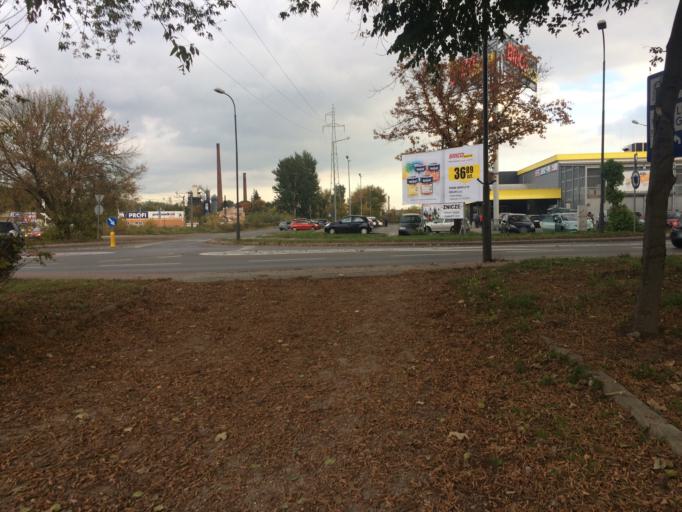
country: PL
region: Swietokrzyskie
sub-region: Powiat starachowicki
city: Starachowice
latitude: 51.0500
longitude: 21.0601
